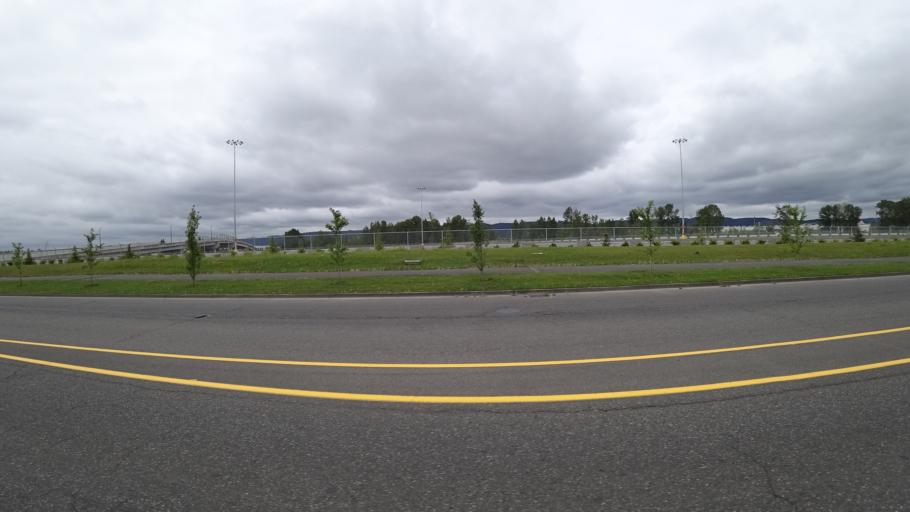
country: US
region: Washington
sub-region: Clark County
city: Lake Shore
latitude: 45.6370
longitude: -122.7573
